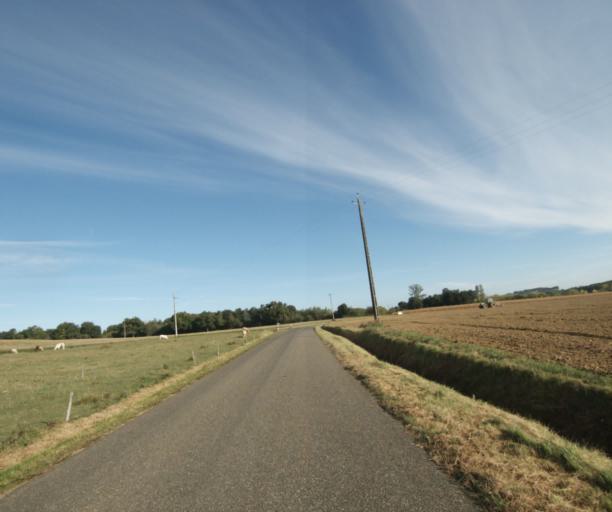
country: FR
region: Midi-Pyrenees
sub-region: Departement du Gers
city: Eauze
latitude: 43.9008
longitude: 0.1375
